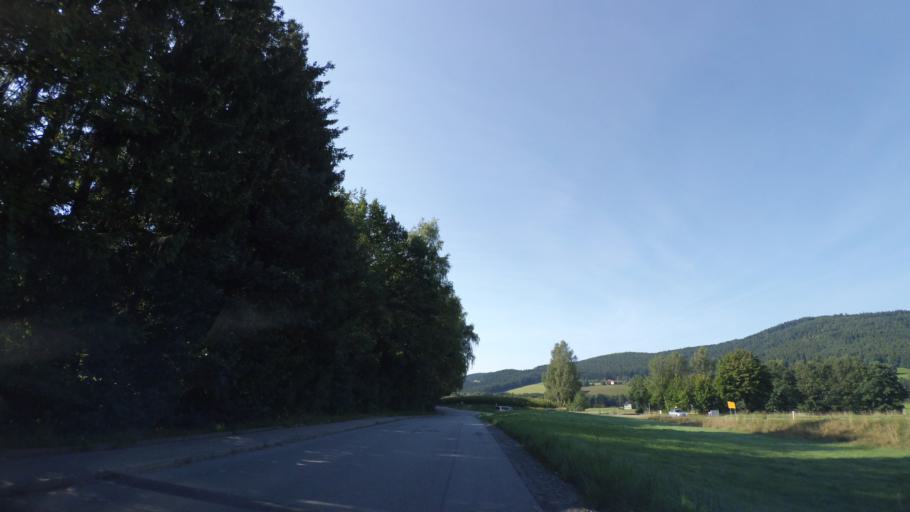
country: DE
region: Bavaria
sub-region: Lower Bavaria
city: Arnbruck
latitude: 49.1218
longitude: 12.9991
